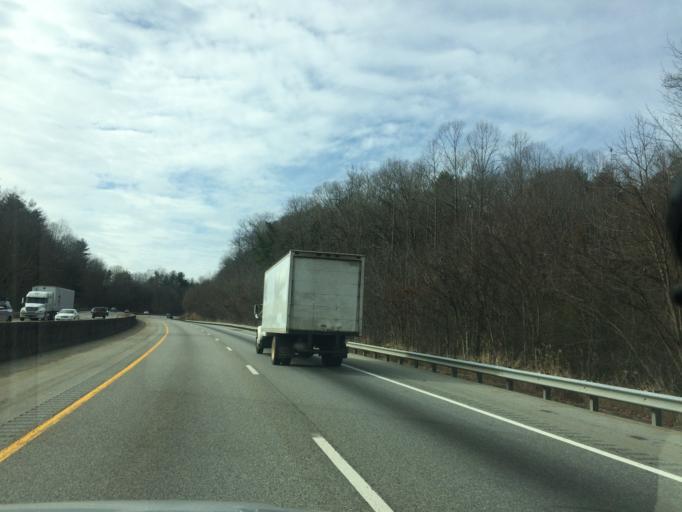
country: US
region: North Carolina
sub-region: Henderson County
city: East Flat Rock
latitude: 35.2765
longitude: -82.3806
